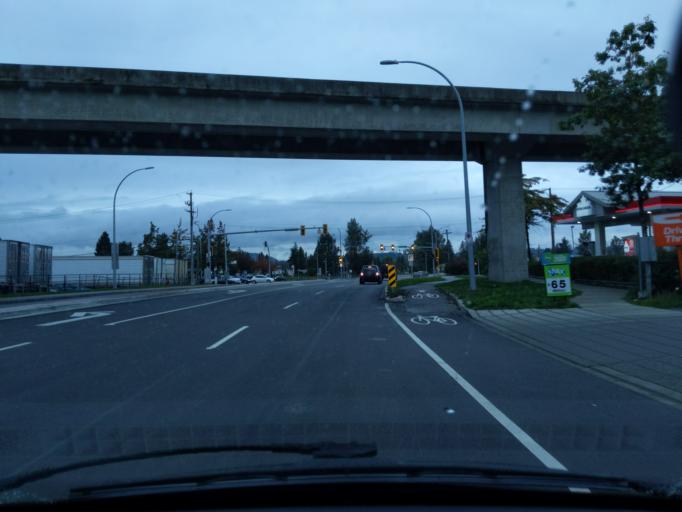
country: CA
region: British Columbia
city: New Westminster
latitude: 49.2054
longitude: -122.8673
